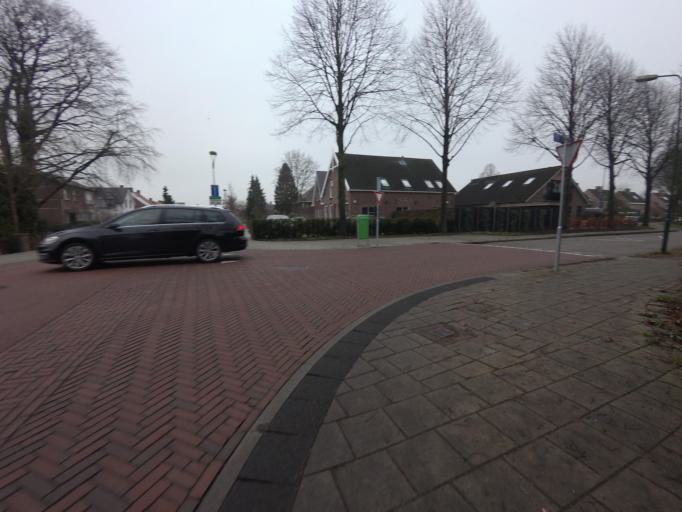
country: NL
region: Utrecht
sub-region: Gemeente Houten
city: Houten
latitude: 52.0260
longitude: 5.1660
